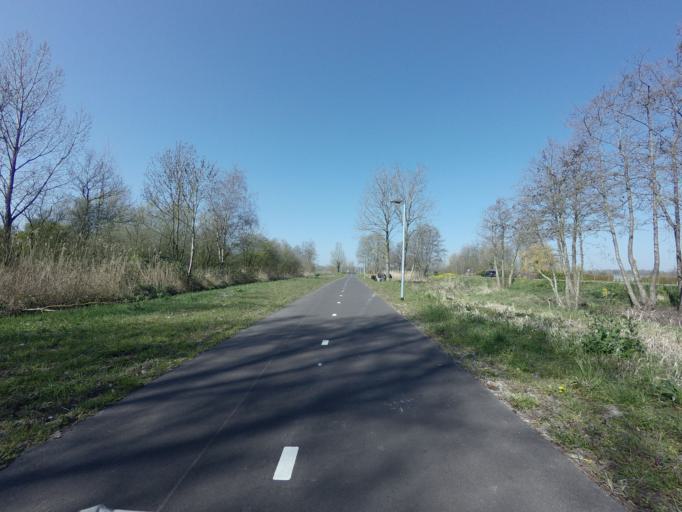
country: NL
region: South Holland
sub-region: Gemeente Alphen aan den Rijn
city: Alphen aan den Rijn
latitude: 52.1325
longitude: 4.7057
